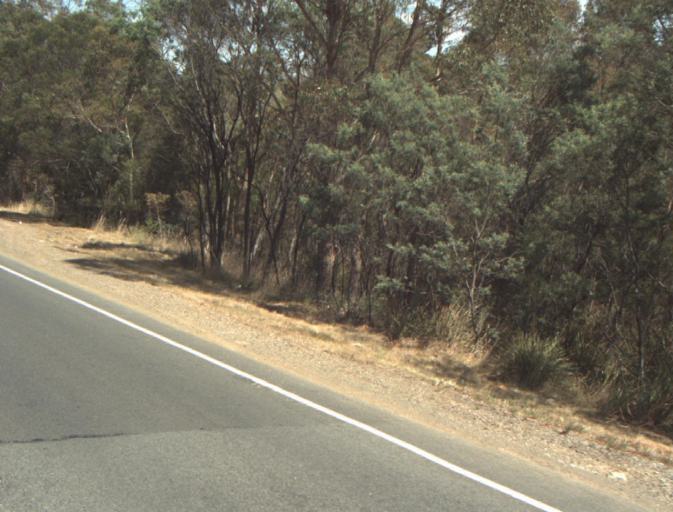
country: AU
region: Tasmania
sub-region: Launceston
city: Mayfield
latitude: -41.3517
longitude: 147.1434
